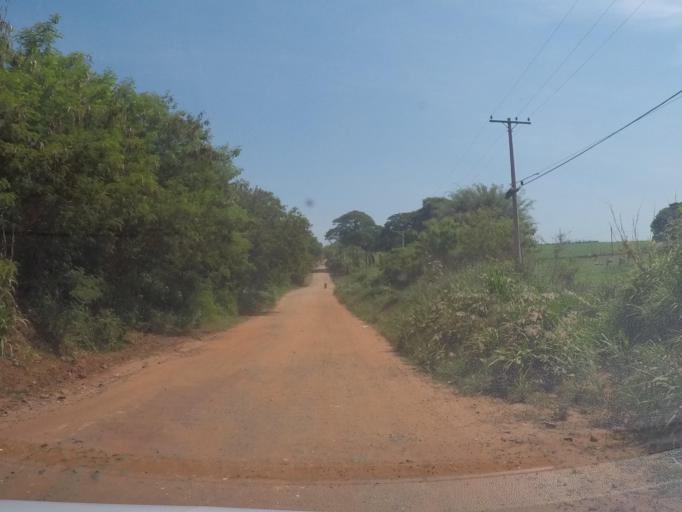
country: BR
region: Sao Paulo
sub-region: Sumare
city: Sumare
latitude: -22.8467
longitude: -47.2711
